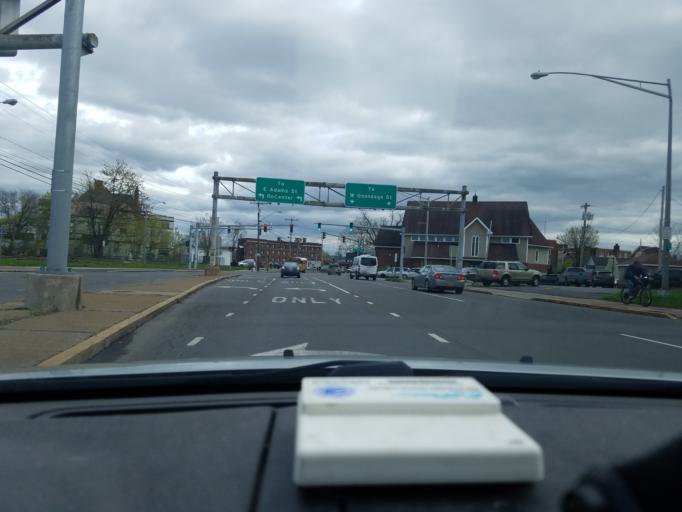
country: US
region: New York
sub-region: Onondaga County
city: Syracuse
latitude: 43.0423
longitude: -76.1579
